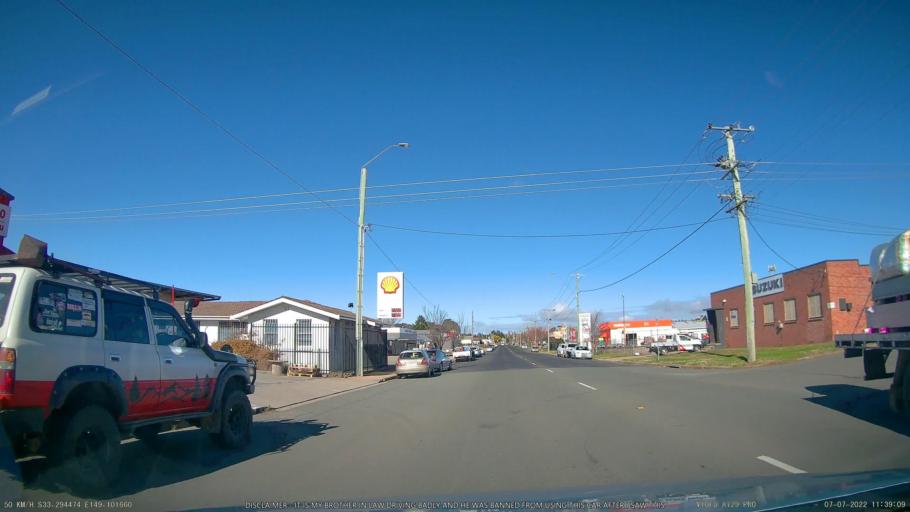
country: AU
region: New South Wales
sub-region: Orange Municipality
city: Orange
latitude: -33.2946
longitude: 149.1017
